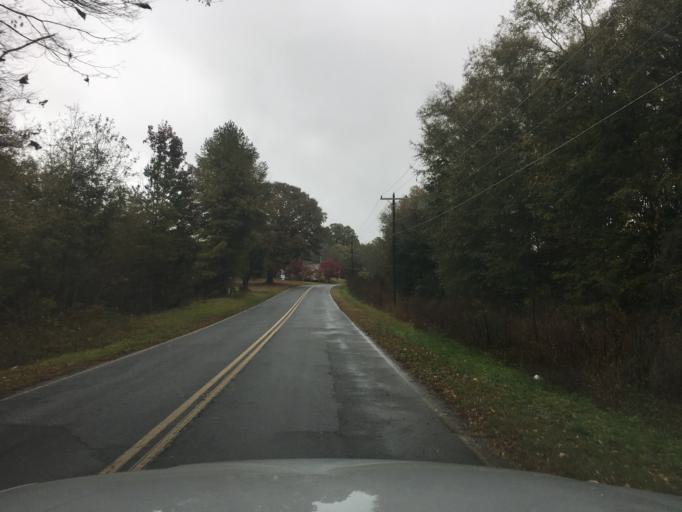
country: US
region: South Carolina
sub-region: Pickens County
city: Central
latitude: 34.7630
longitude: -82.7571
